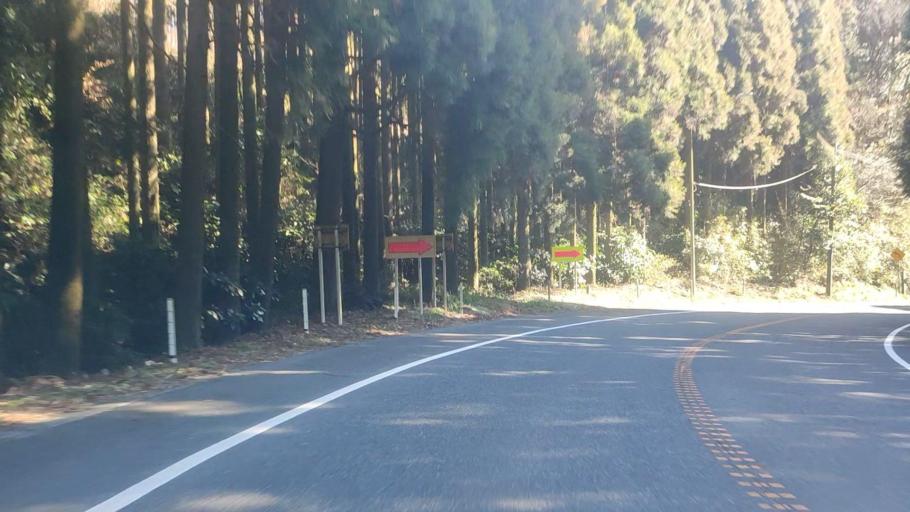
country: JP
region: Kagoshima
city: Sueyoshicho-ninokata
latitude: 31.6637
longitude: 130.8835
